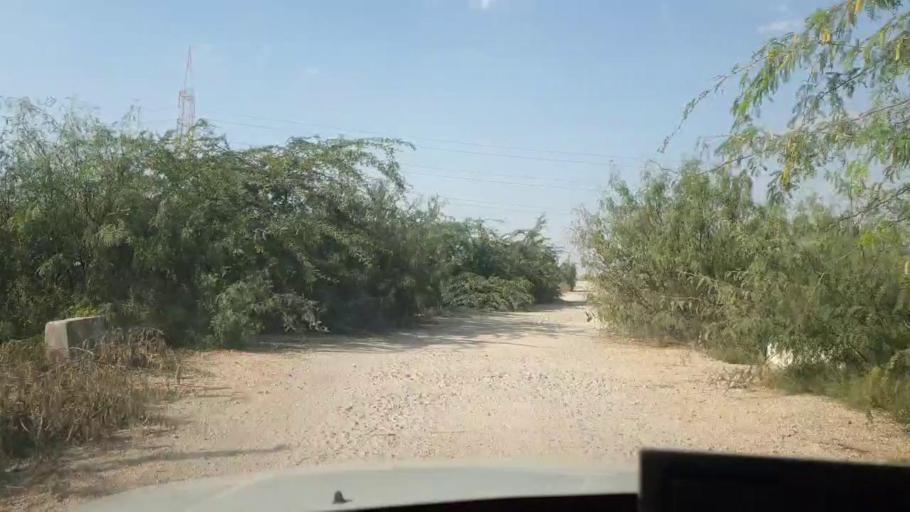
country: PK
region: Sindh
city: Daro Mehar
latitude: 25.0698
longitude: 68.0976
